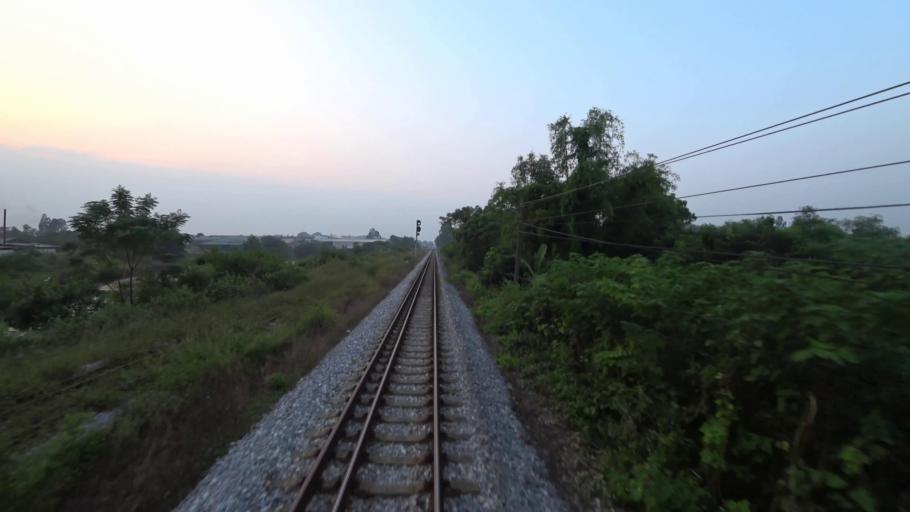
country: VN
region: Ha Noi
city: Dong Anh
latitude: 21.1372
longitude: 105.8692
